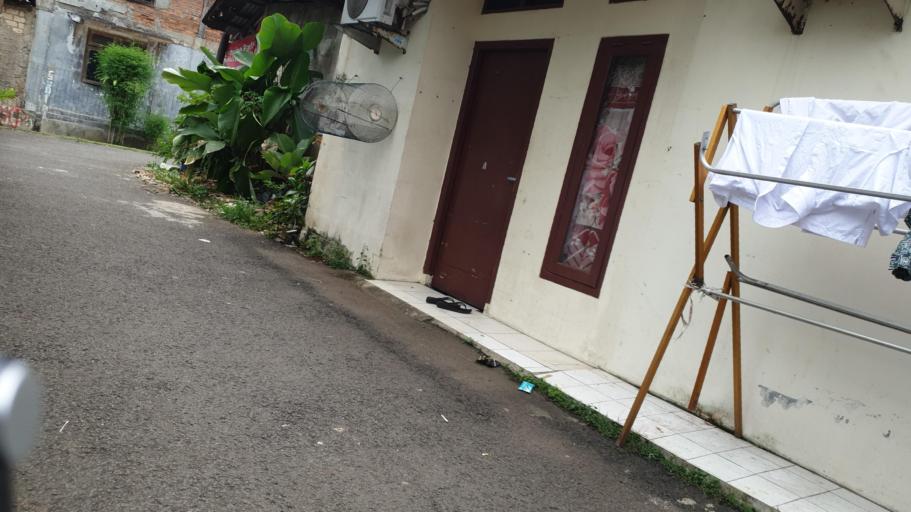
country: ID
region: West Java
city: Pamulang
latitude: -6.3046
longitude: 106.7804
